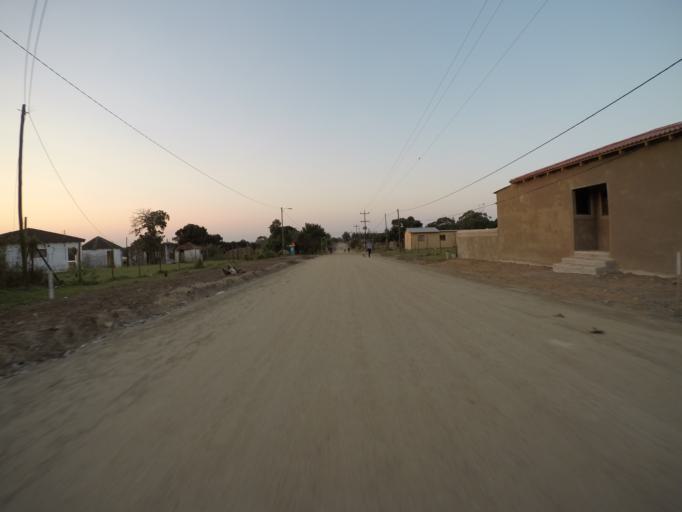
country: ZA
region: KwaZulu-Natal
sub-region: uThungulu District Municipality
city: Richards Bay
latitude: -28.7592
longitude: 32.1282
